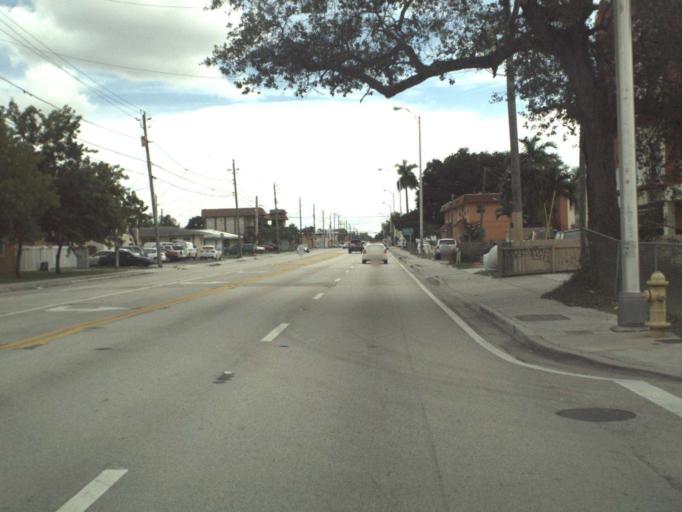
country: US
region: Florida
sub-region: Miami-Dade County
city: West Miami
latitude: 25.7744
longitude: -80.2883
